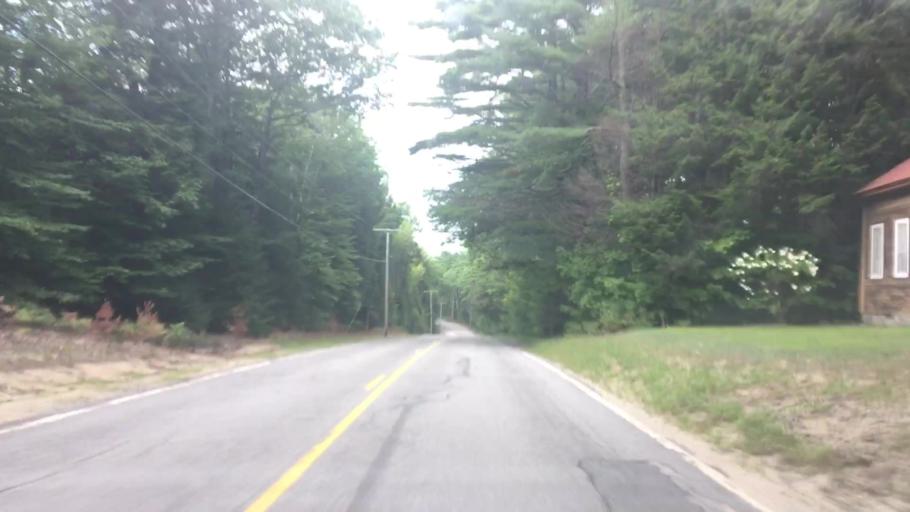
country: US
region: Maine
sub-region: Oxford County
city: Oxford
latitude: 44.0272
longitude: -70.5306
